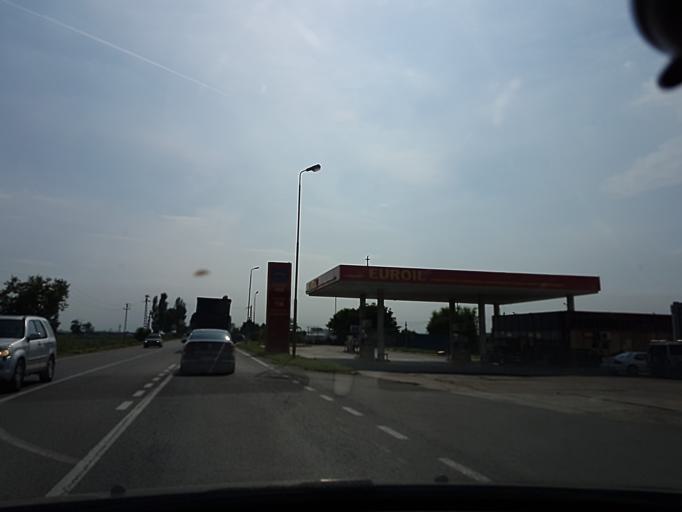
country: RO
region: Prahova
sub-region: Comuna Blejoiu
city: Ploiestiori
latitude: 44.9837
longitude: 26.0045
